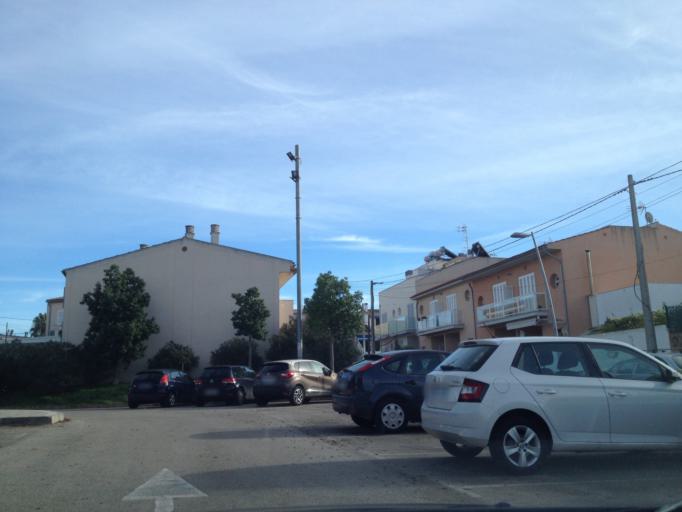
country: ES
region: Balearic Islands
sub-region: Illes Balears
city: Marratxi
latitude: 39.6244
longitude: 2.7256
